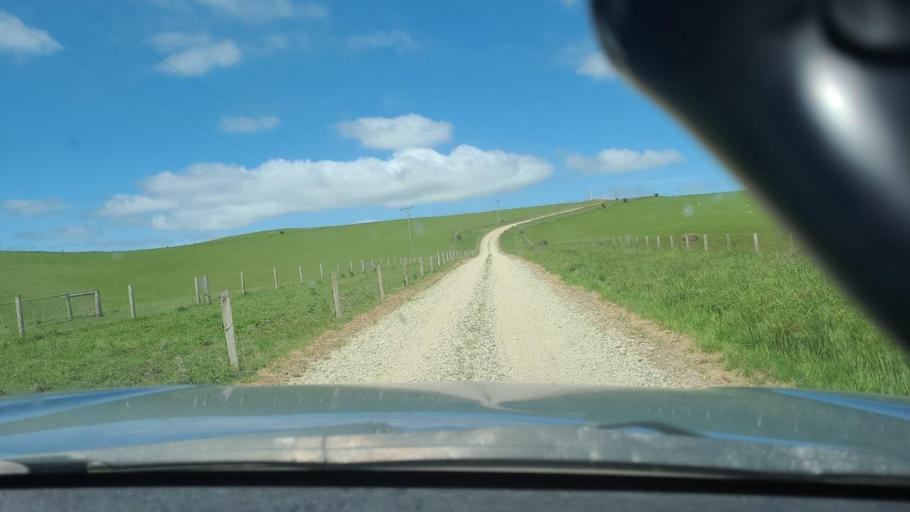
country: NZ
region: Southland
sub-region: Gore District
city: Gore
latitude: -46.3727
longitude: 168.9492
